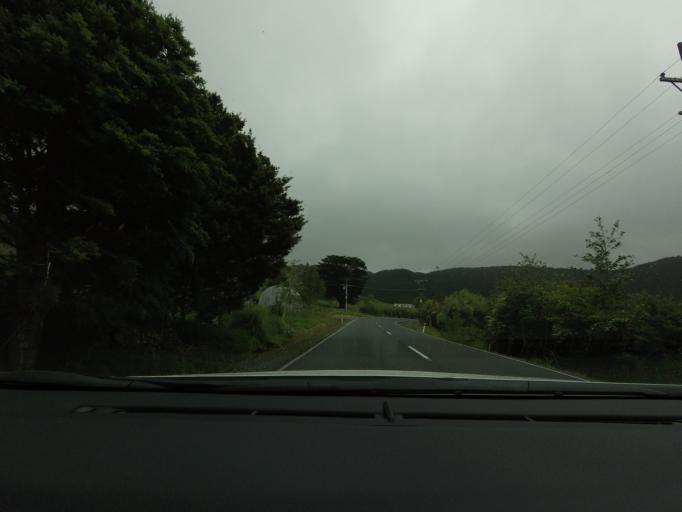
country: NZ
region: Auckland
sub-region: Auckland
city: Wellsford
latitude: -36.2935
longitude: 174.6218
